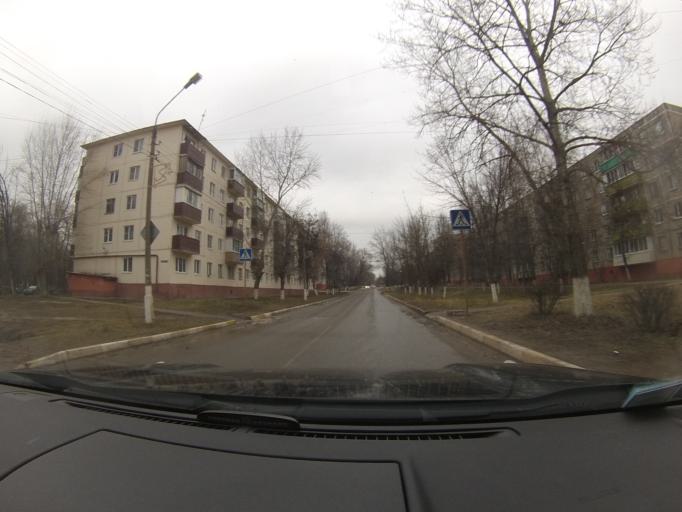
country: RU
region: Moskovskaya
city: Peski
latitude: 55.2729
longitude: 38.7480
